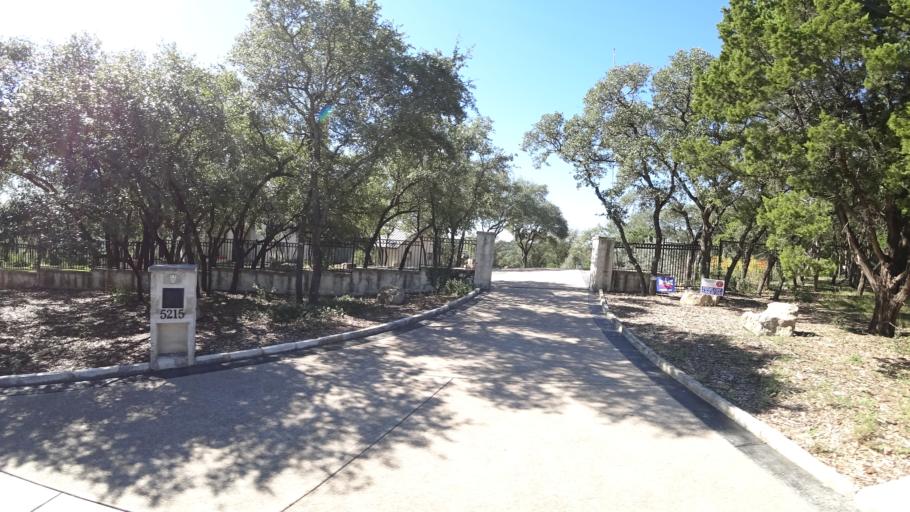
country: US
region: Texas
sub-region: Travis County
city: West Lake Hills
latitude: 30.3234
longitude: -97.7978
